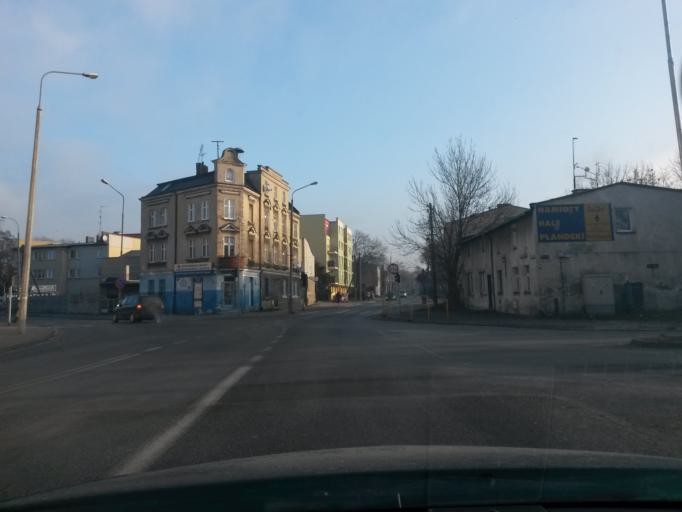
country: PL
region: Greater Poland Voivodeship
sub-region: Powiat poznanski
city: Czerwonak
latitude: 52.4223
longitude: 16.9757
